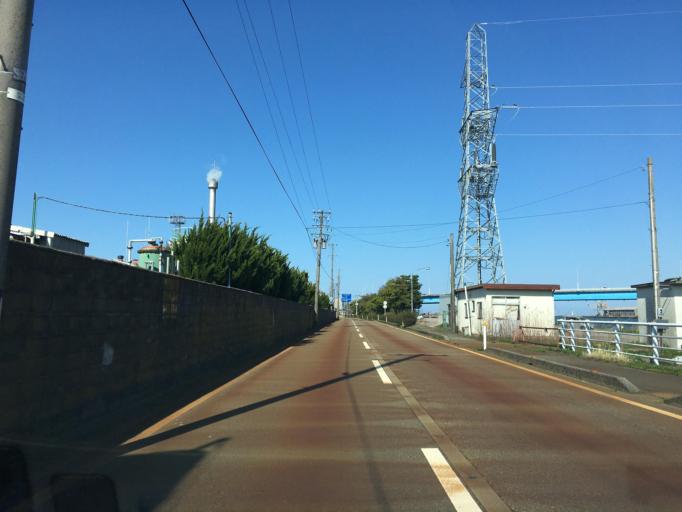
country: JP
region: Toyama
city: Nishishinminato
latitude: 36.7884
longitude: 137.0555
